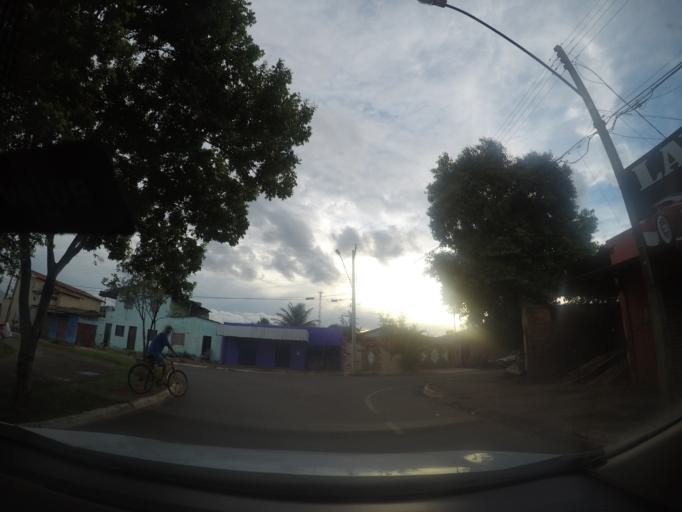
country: BR
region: Goias
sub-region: Goianira
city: Goianira
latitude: -16.5889
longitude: -49.3768
